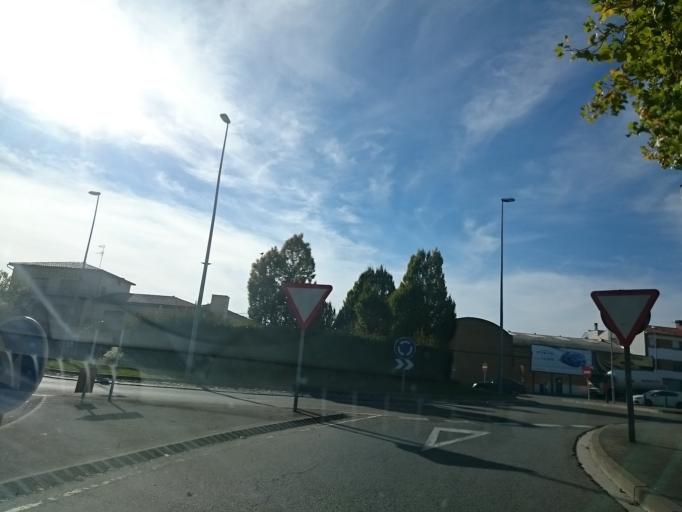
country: ES
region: Catalonia
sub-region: Provincia de Barcelona
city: Vic
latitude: 41.9278
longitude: 2.2455
